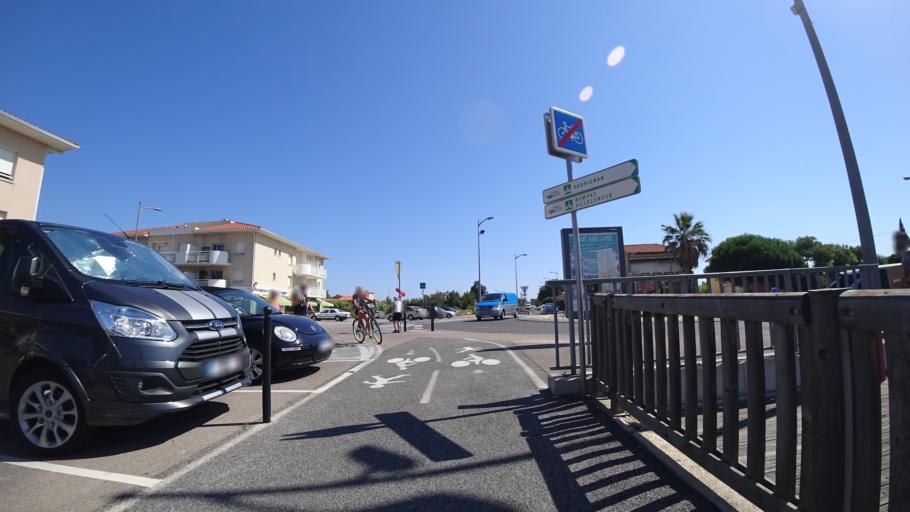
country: FR
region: Languedoc-Roussillon
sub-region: Departement des Pyrenees-Orientales
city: Sainte-Marie-Plage
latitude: 42.7289
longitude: 3.0214
